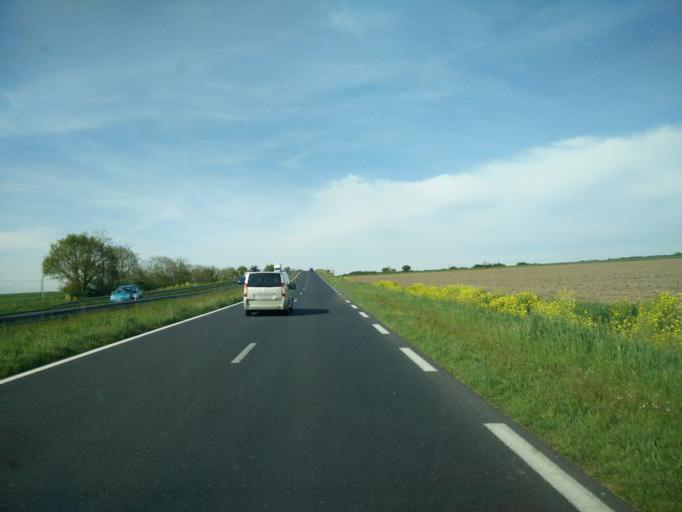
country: FR
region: Lower Normandy
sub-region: Departement de la Manche
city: Pontorson
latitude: 48.5833
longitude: -1.4362
